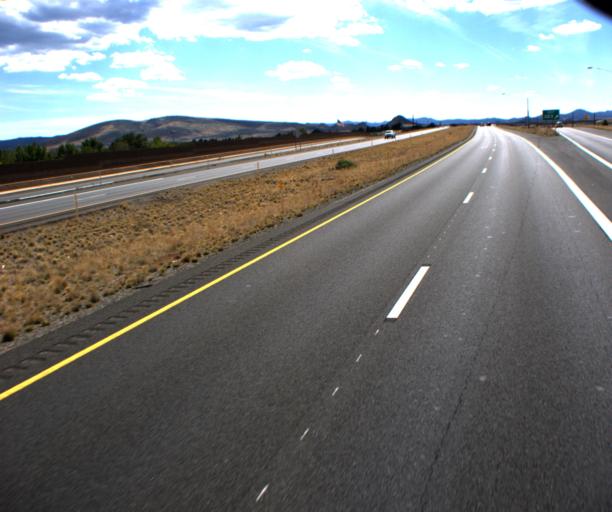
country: US
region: Arizona
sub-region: Yavapai County
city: Prescott Valley
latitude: 34.6384
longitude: -112.3281
